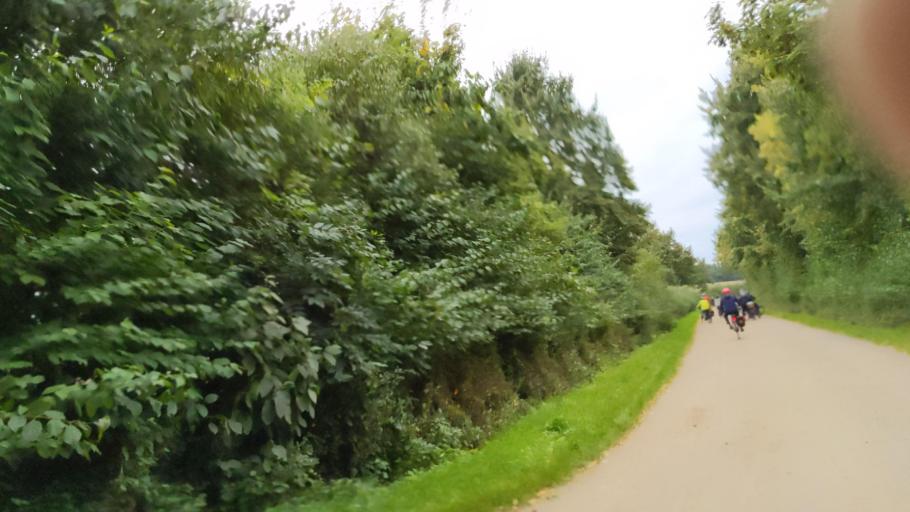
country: DE
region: Schleswig-Holstein
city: Buchholz
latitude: 53.7528
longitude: 10.7607
